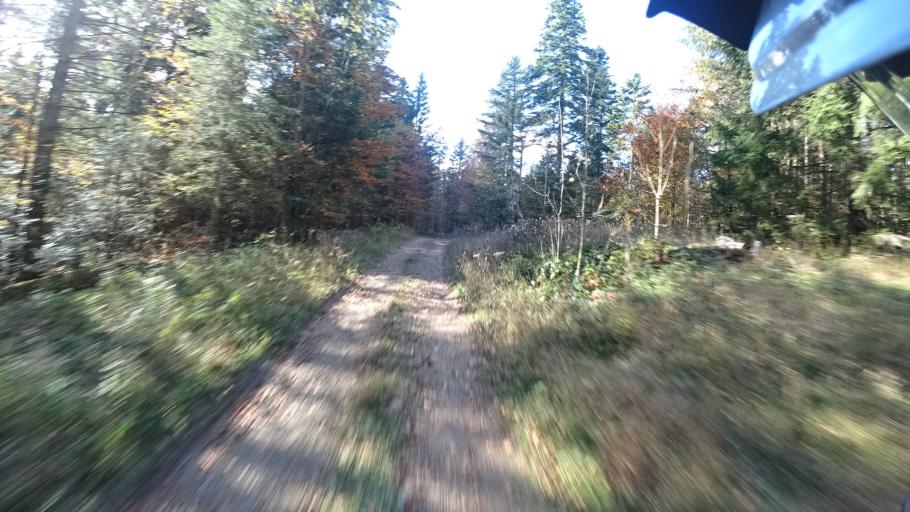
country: HR
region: Karlovacka
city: Plaski
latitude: 45.0431
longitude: 15.3393
